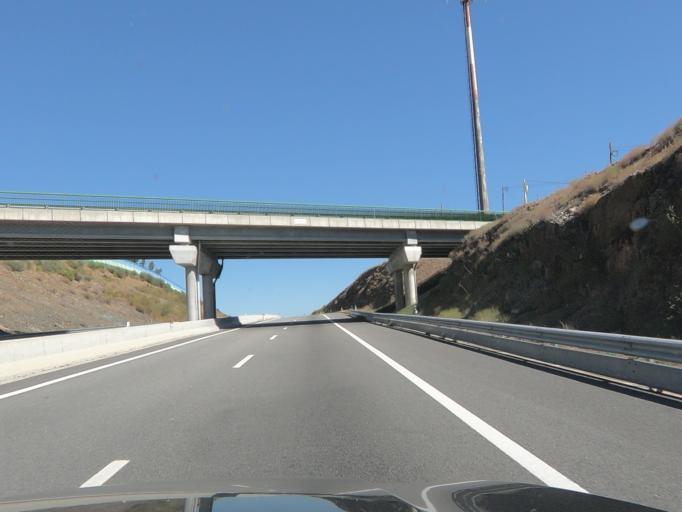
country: PT
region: Braganca
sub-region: Mirandela
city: Mirandela
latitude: 41.4392
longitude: -7.3120
